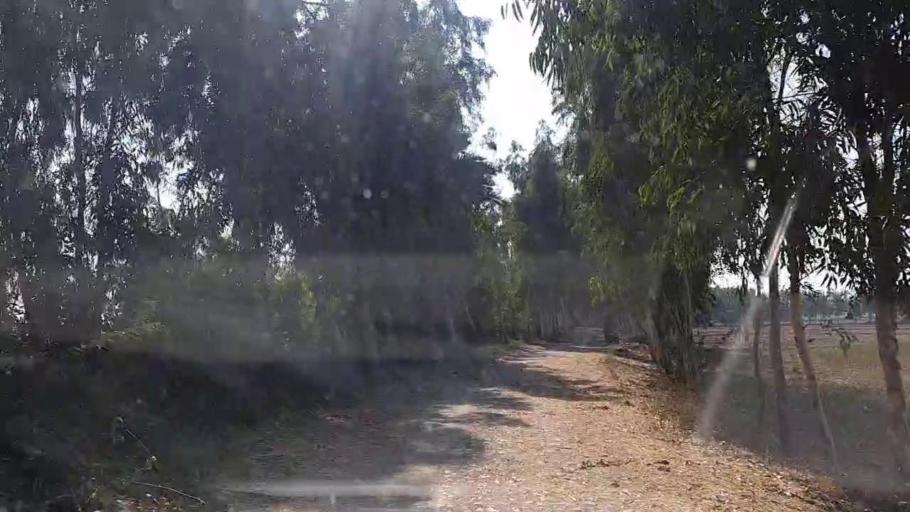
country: PK
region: Sindh
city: Thatta
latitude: 24.7981
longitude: 67.9685
